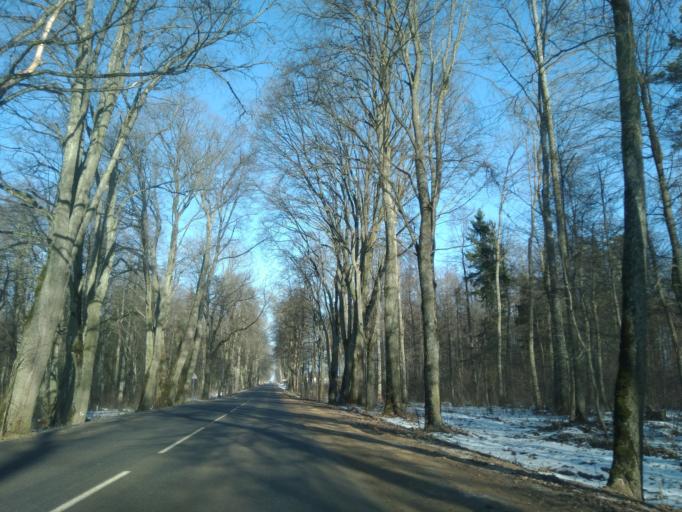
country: BY
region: Minsk
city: Nyasvizh
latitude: 53.2019
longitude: 26.6566
